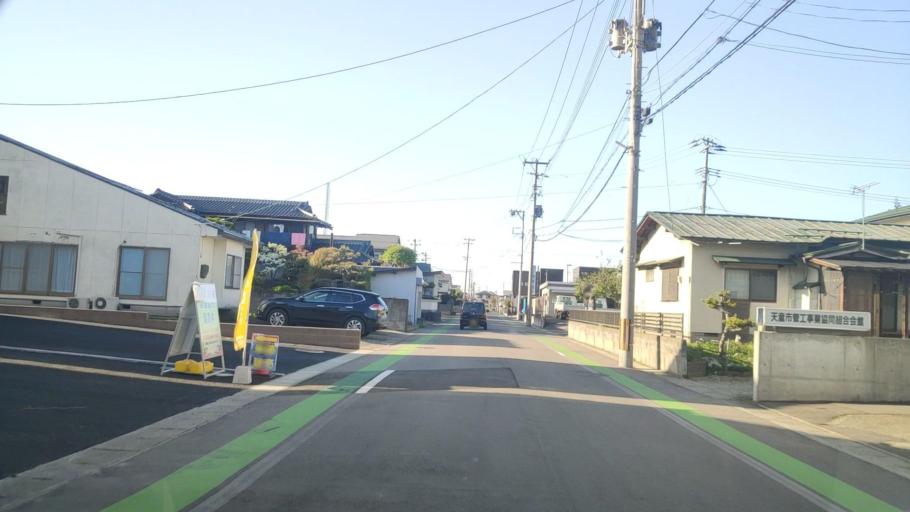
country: JP
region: Yamagata
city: Tendo
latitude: 38.3632
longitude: 140.3844
